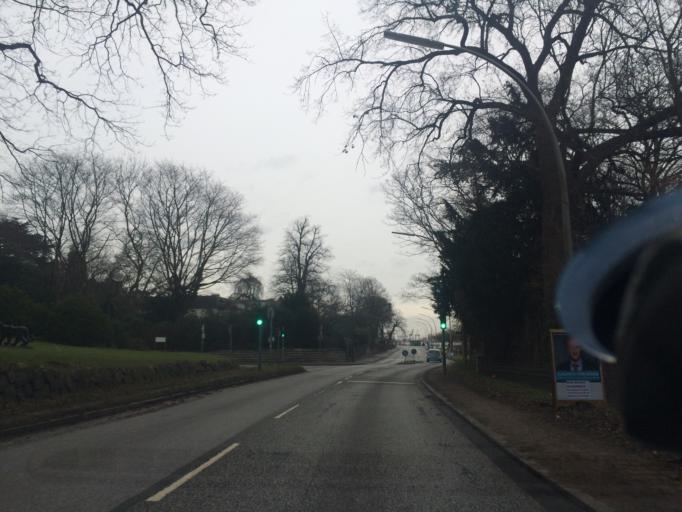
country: DE
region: Hamburg
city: Altona
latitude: 53.5483
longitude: 9.8584
